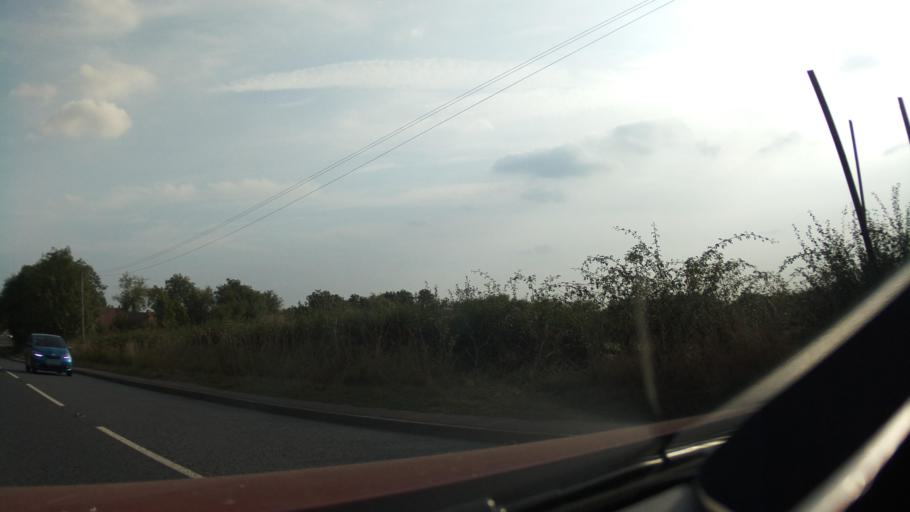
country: GB
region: England
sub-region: Gloucestershire
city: Gotherington
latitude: 51.9574
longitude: -2.0670
